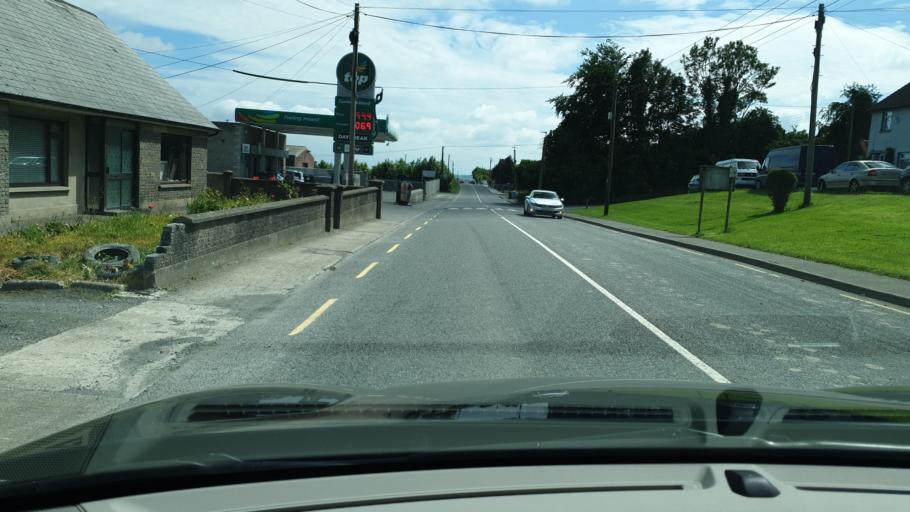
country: IE
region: Ulster
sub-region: An Cabhan
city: Kingscourt
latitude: 53.9006
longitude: -6.8035
